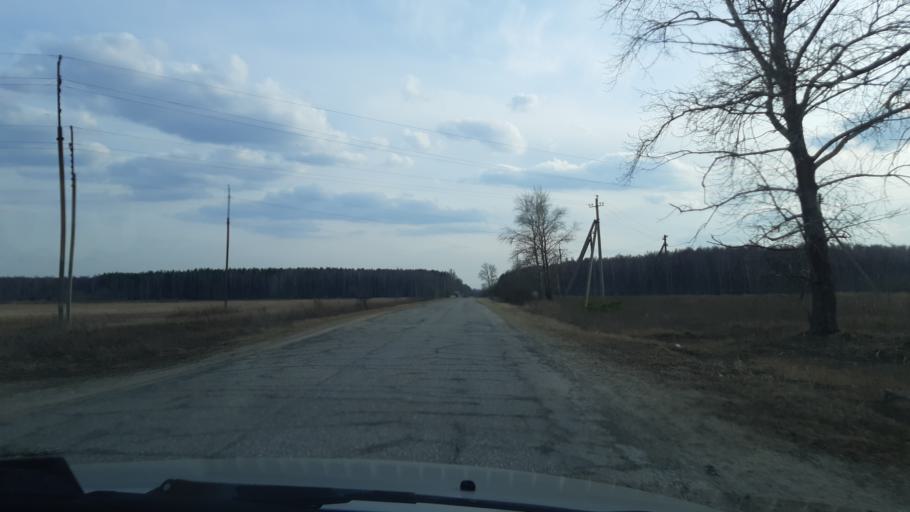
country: RU
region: Vladimir
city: Nikologory
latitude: 56.1239
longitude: 41.9878
